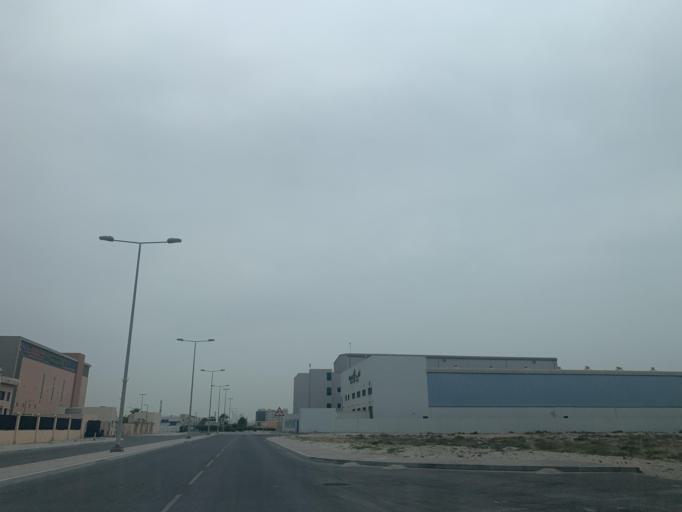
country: BH
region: Muharraq
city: Al Hadd
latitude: 26.2134
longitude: 50.6814
